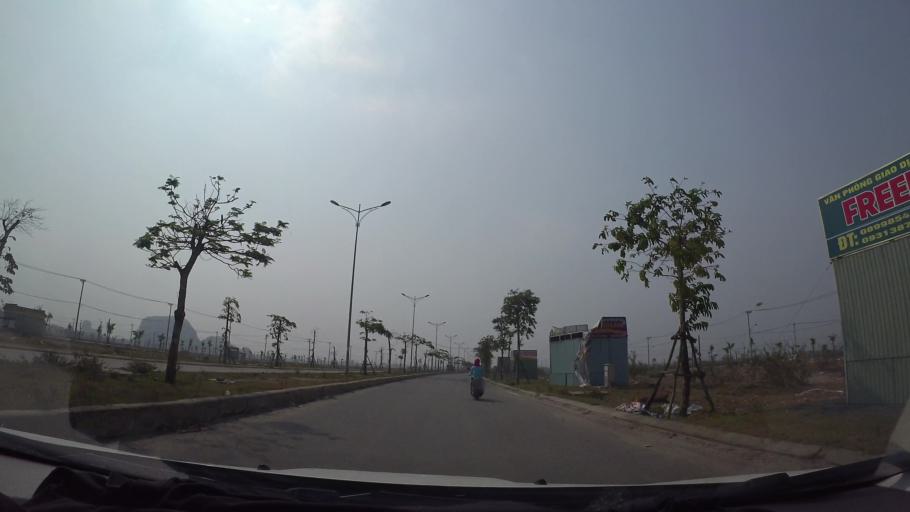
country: VN
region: Da Nang
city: Ngu Hanh Son
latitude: 16.0061
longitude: 108.2456
